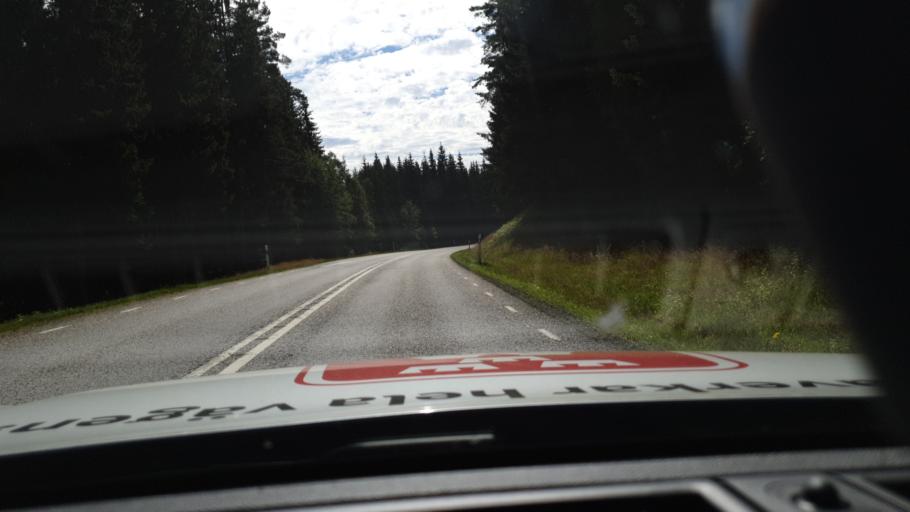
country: SE
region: Joenkoeping
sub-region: Vaggeryds Kommun
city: Vaggeryd
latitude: 57.5566
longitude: 14.2610
